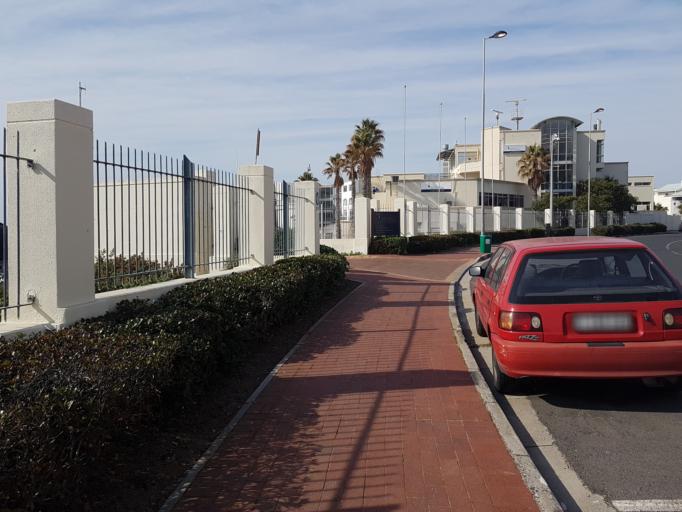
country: ZA
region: Western Cape
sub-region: City of Cape Town
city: Cape Town
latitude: -33.8994
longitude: 18.4106
